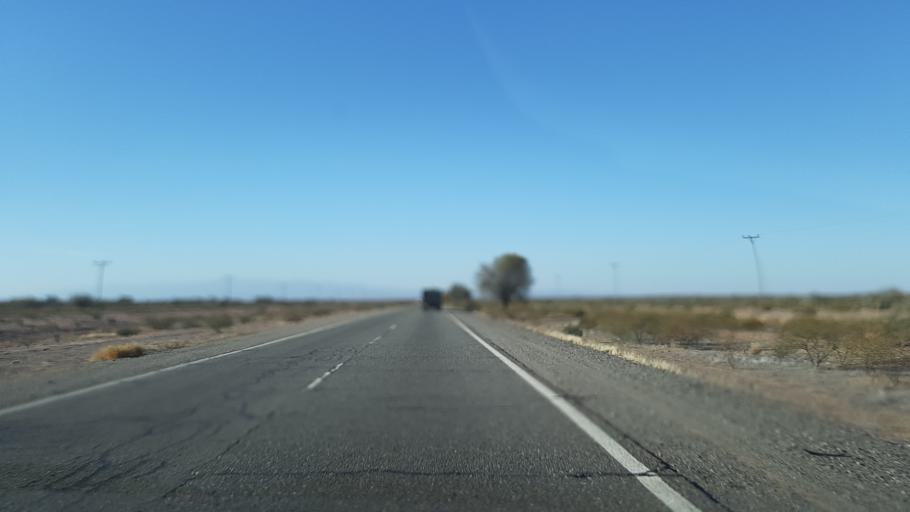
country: AR
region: San Juan
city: Caucete
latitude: -31.6568
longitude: -67.7719
